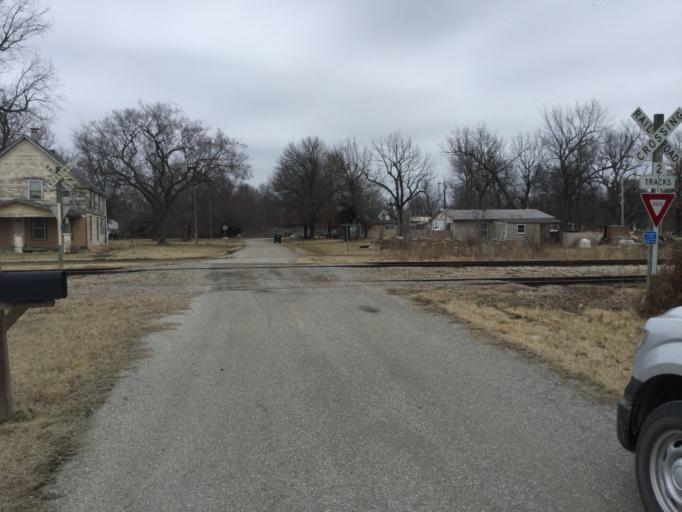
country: US
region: Kansas
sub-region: Labette County
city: Oswego
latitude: 37.1739
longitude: -94.9985
